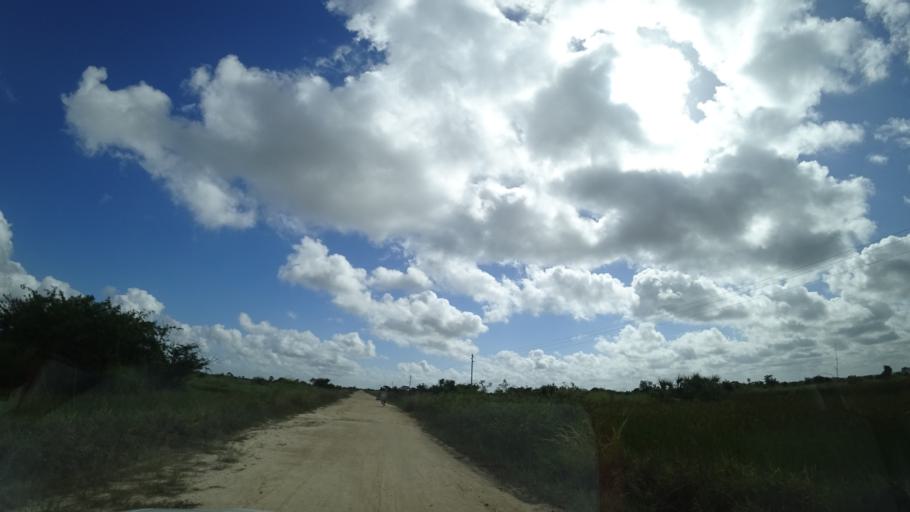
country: MZ
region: Sofala
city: Dondo
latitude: -19.4416
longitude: 34.5618
